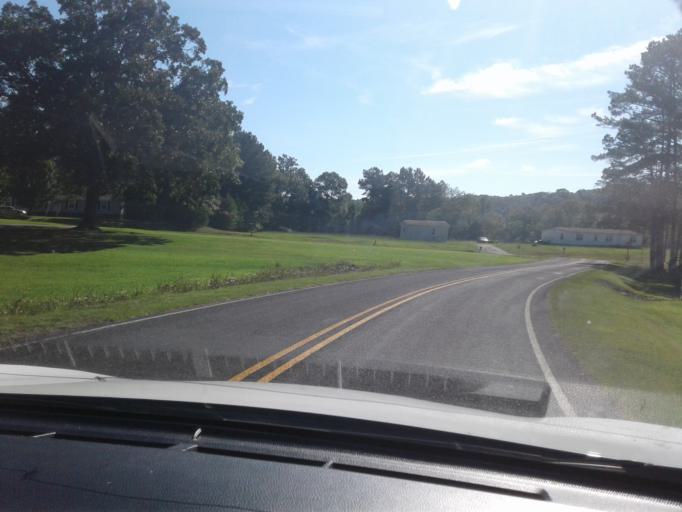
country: US
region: North Carolina
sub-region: Harnett County
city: Lillington
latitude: 35.4675
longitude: -78.8607
